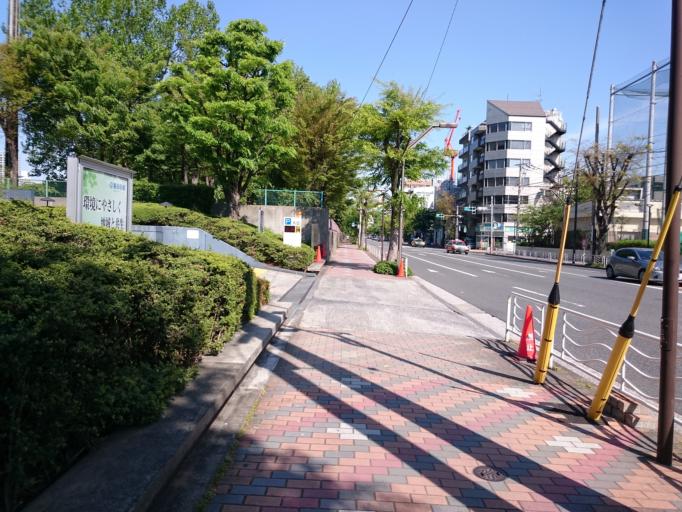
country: JP
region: Tokyo
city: Urayasu
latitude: 35.6656
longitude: 139.7953
